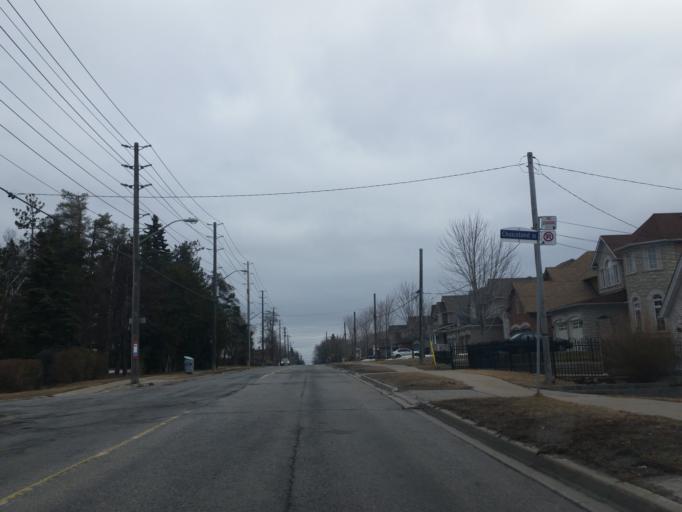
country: CA
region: Ontario
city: Scarborough
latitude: 43.7870
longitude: -79.1649
